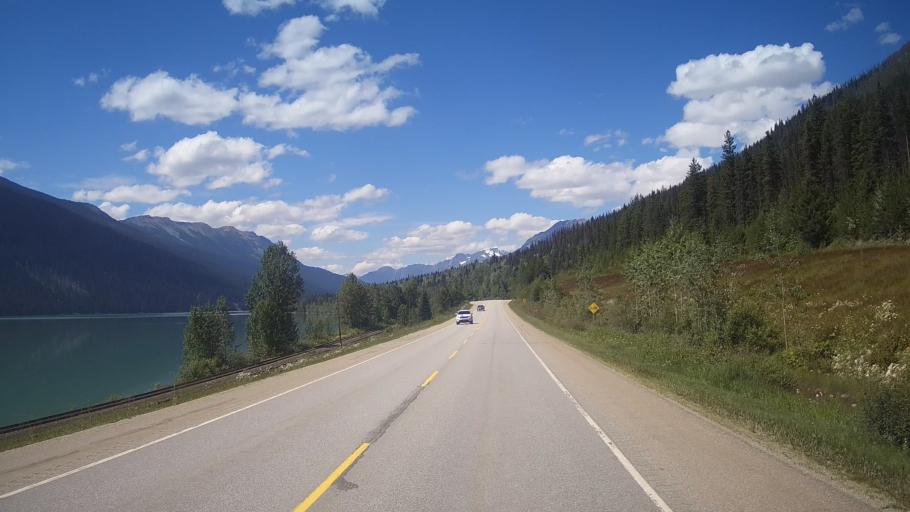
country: CA
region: Alberta
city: Jasper Park Lodge
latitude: 52.9687
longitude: -118.9298
